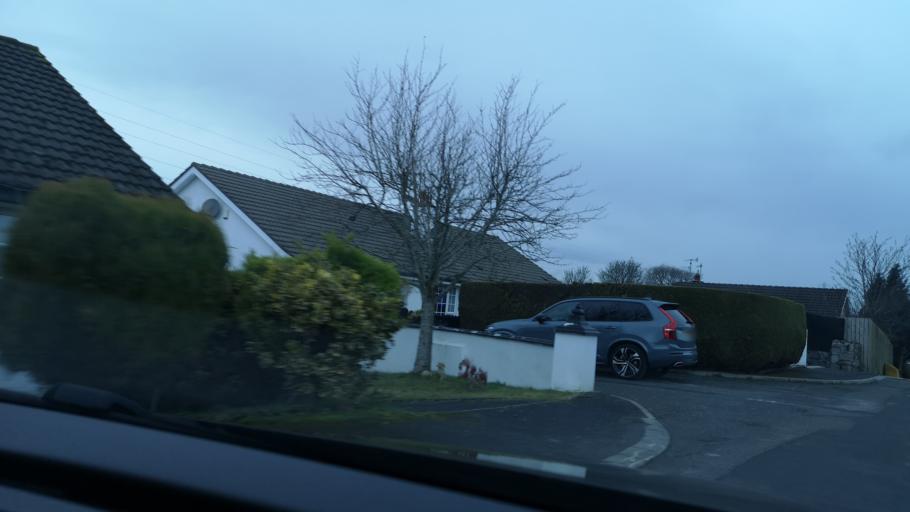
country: GB
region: Northern Ireland
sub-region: Newry and Mourne District
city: Newry
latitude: 54.1909
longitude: -6.3208
